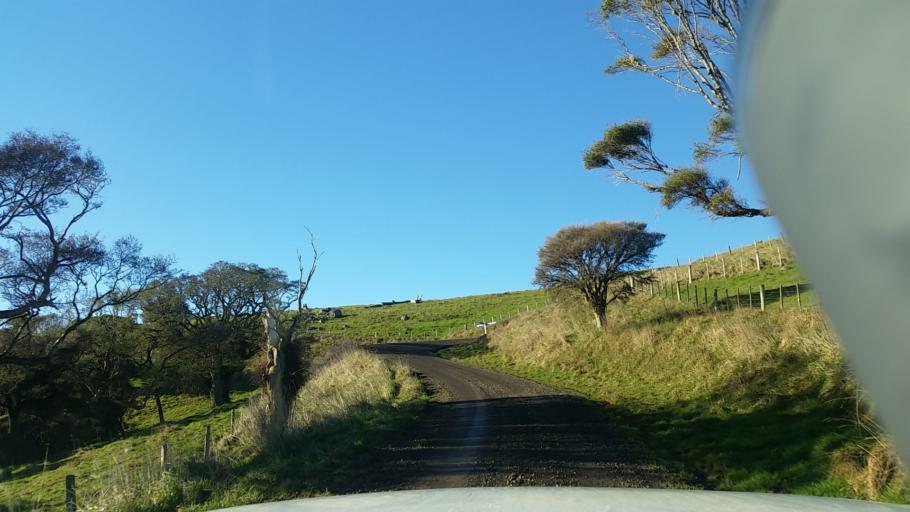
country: NZ
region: Canterbury
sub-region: Christchurch City
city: Christchurch
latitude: -43.7231
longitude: 173.0513
